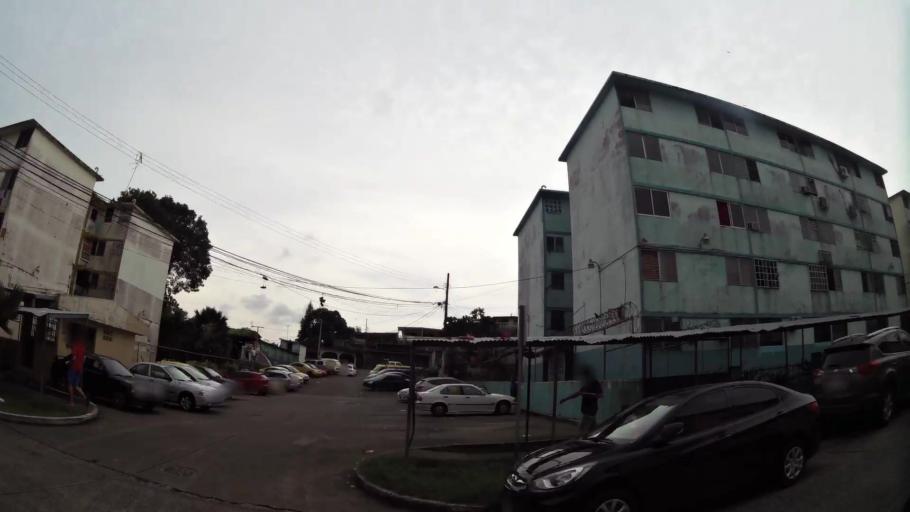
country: PA
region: Panama
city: Panama
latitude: 9.0195
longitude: -79.5297
